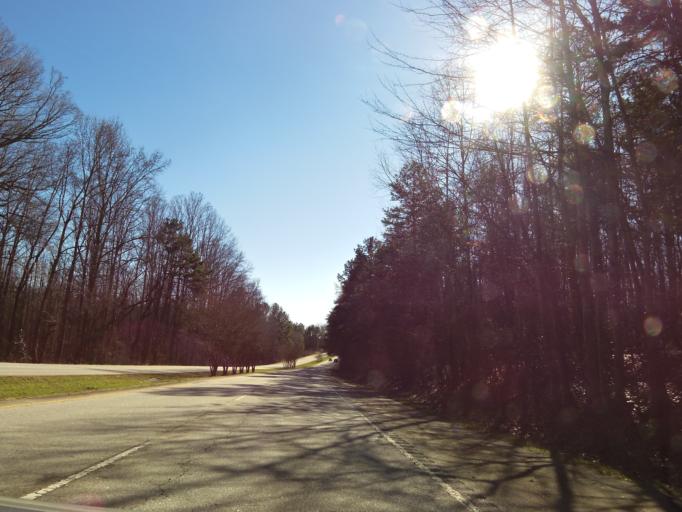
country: US
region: South Carolina
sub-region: Greenville County
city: Travelers Rest
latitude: 34.9356
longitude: -82.4338
